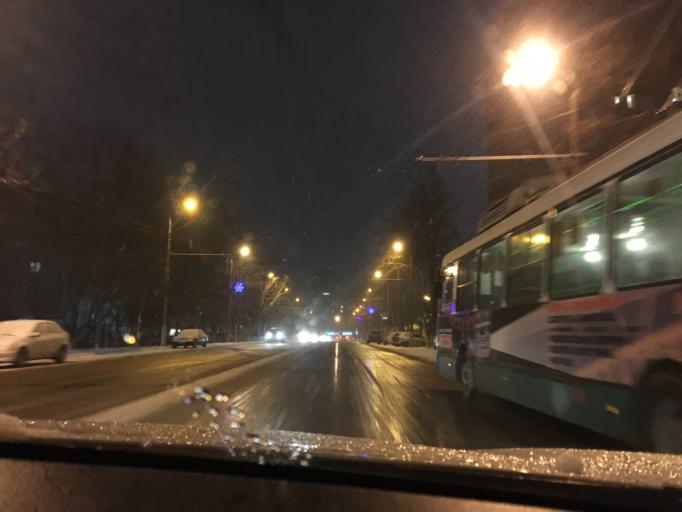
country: RU
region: Tula
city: Mendeleyevskiy
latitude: 54.1698
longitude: 37.5733
